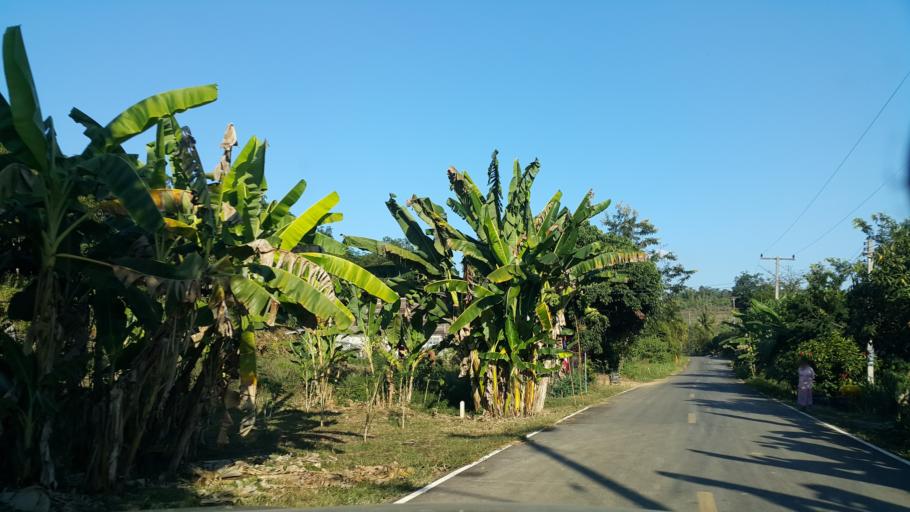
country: TH
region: Sukhothai
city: Thung Saliam
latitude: 17.4068
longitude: 99.5130
